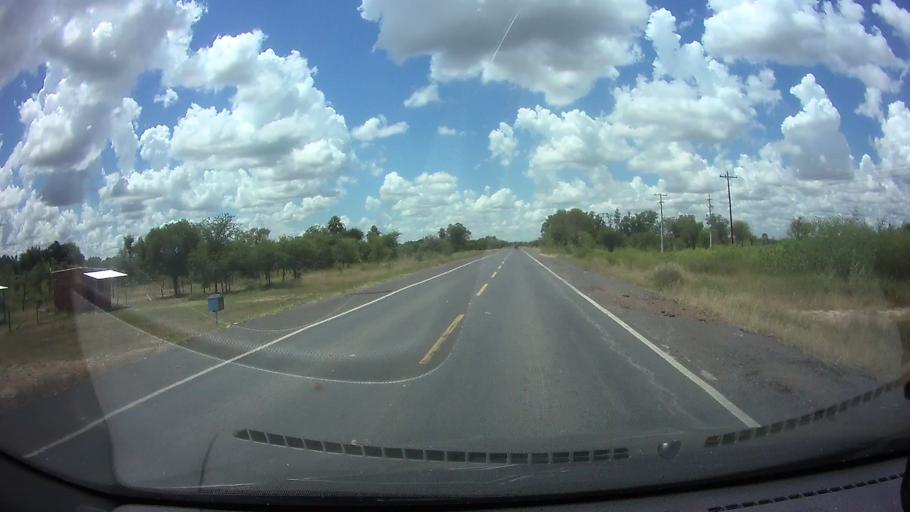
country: PY
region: Presidente Hayes
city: Nanawa
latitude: -25.2162
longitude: -57.6681
